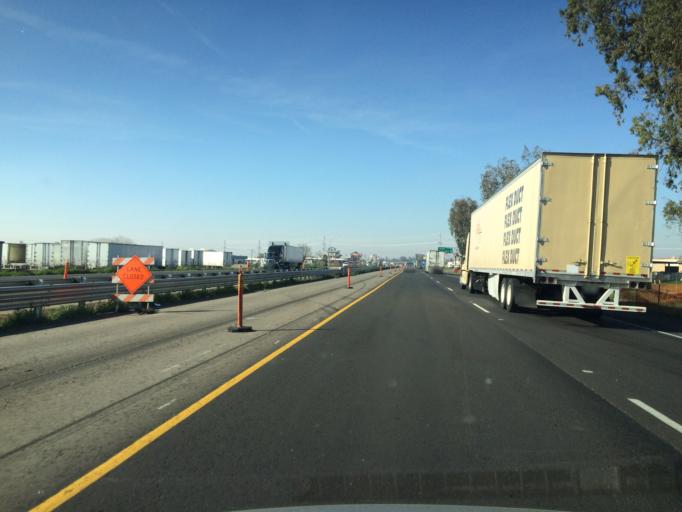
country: US
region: California
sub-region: Tulare County
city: Goshen
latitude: 36.3388
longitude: -119.4173
